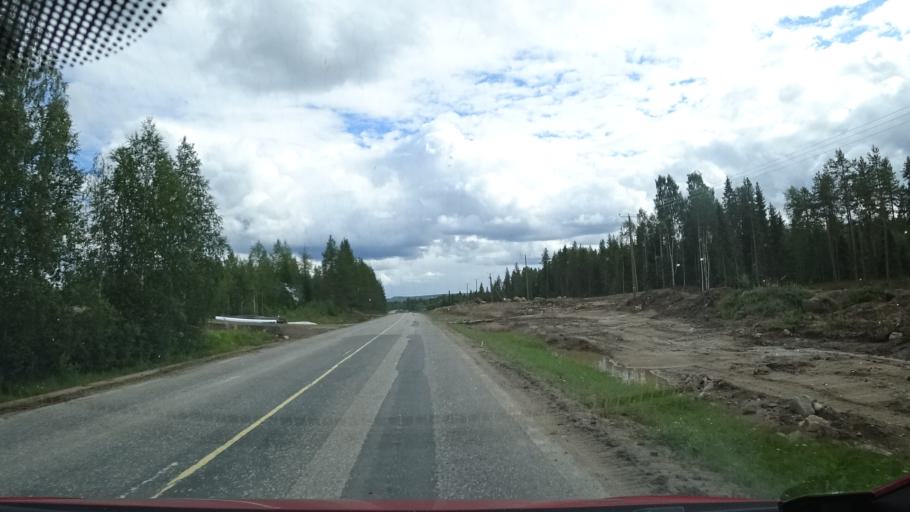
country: FI
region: Lapland
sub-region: Rovaniemi
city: Rovaniemi
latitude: 66.5422
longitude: 25.7140
